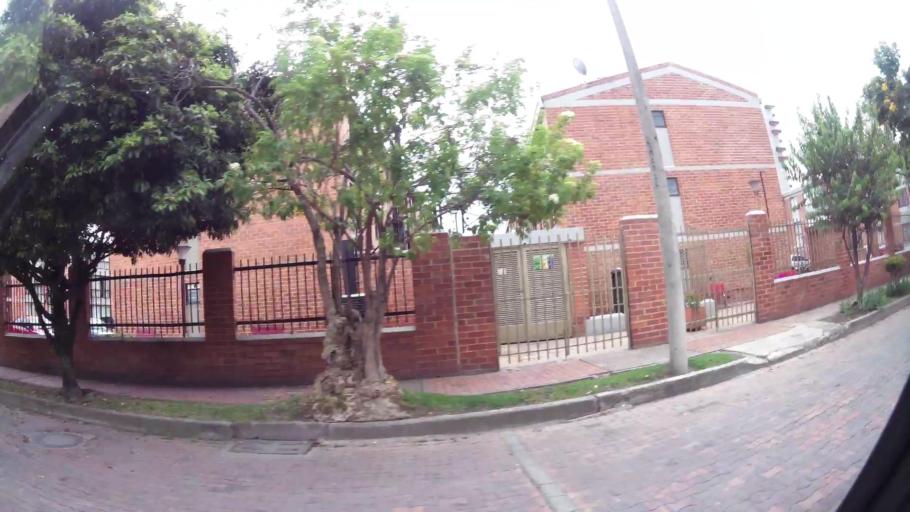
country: CO
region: Cundinamarca
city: Cota
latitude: 4.7478
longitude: -74.0638
